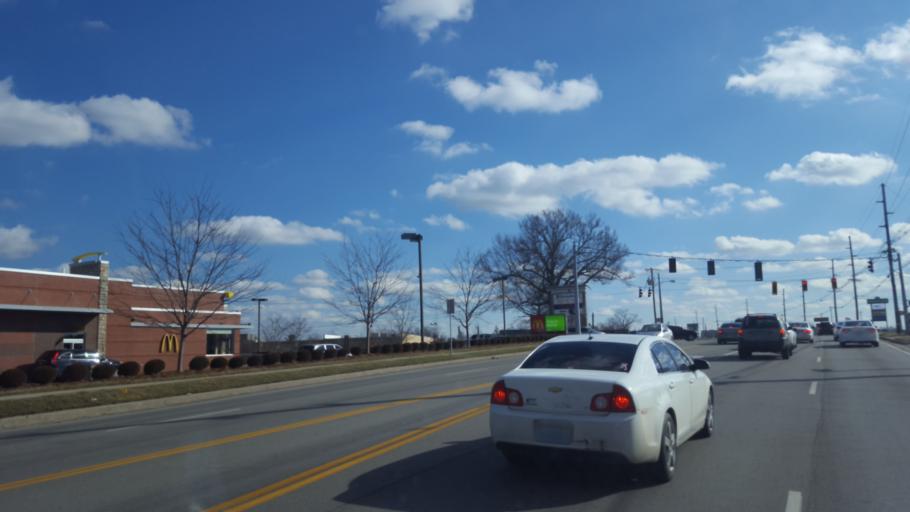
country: US
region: Kentucky
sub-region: Franklin County
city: Frankfort
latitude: 38.1981
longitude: -84.8306
